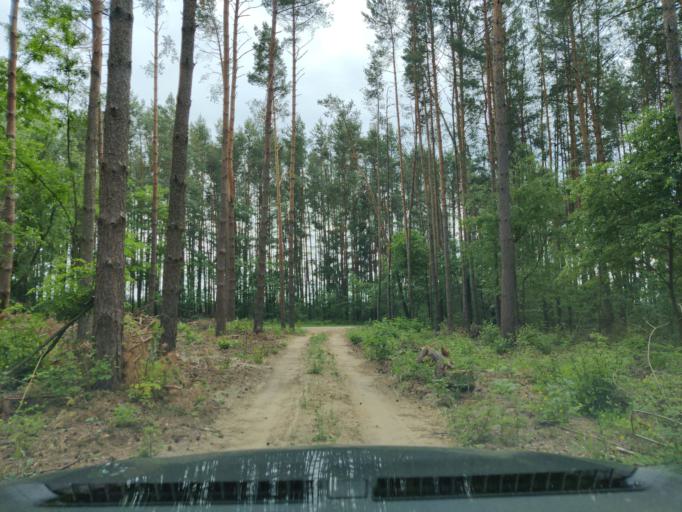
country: PL
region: Masovian Voivodeship
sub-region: Powiat pultuski
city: Obryte
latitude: 52.7517
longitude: 21.2018
